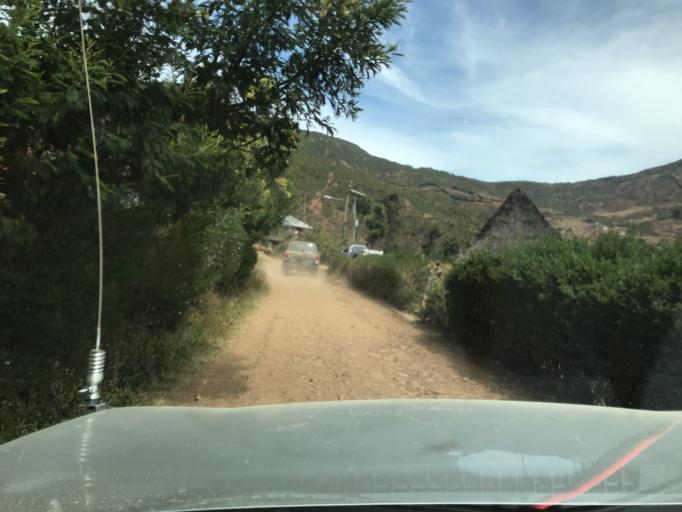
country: TL
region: Ainaro
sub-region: Ainaro
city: Ainaro
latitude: -8.8937
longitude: 125.5188
